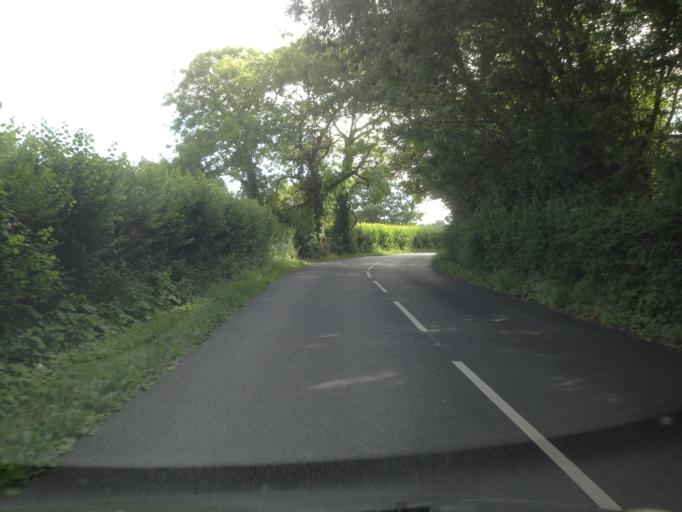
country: GB
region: England
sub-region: Isle of Wight
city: Bembridge
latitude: 50.6797
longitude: -1.0884
